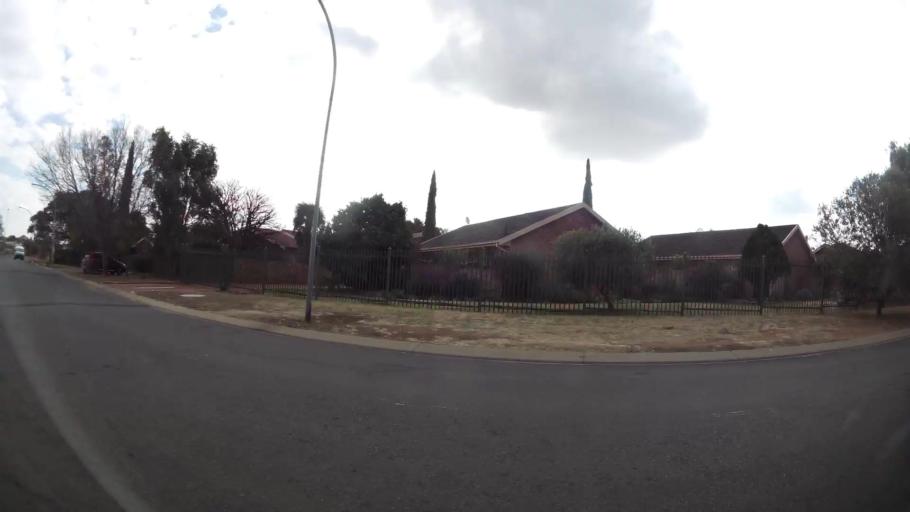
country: ZA
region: Orange Free State
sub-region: Mangaung Metropolitan Municipality
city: Bloemfontein
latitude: -29.0766
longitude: 26.1940
